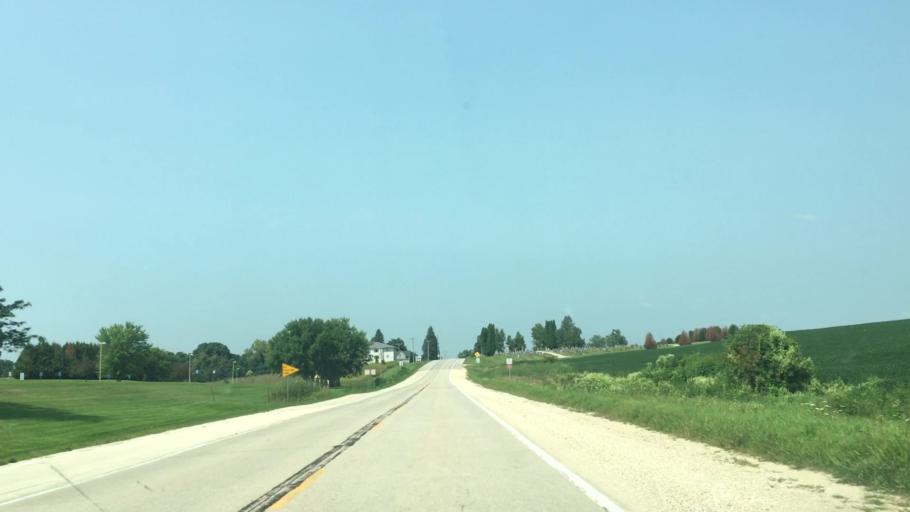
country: US
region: Iowa
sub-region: Winneshiek County
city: Decorah
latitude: 43.1740
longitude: -91.8644
